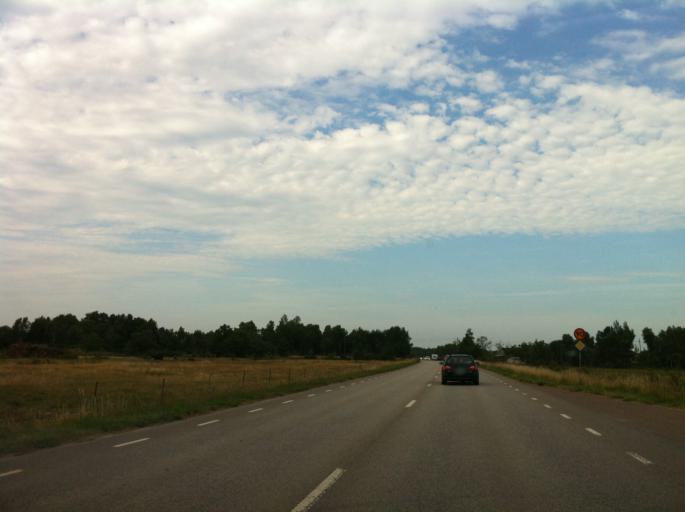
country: SE
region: Kalmar
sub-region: Borgholms Kommun
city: Borgholm
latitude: 57.0084
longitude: 16.8433
